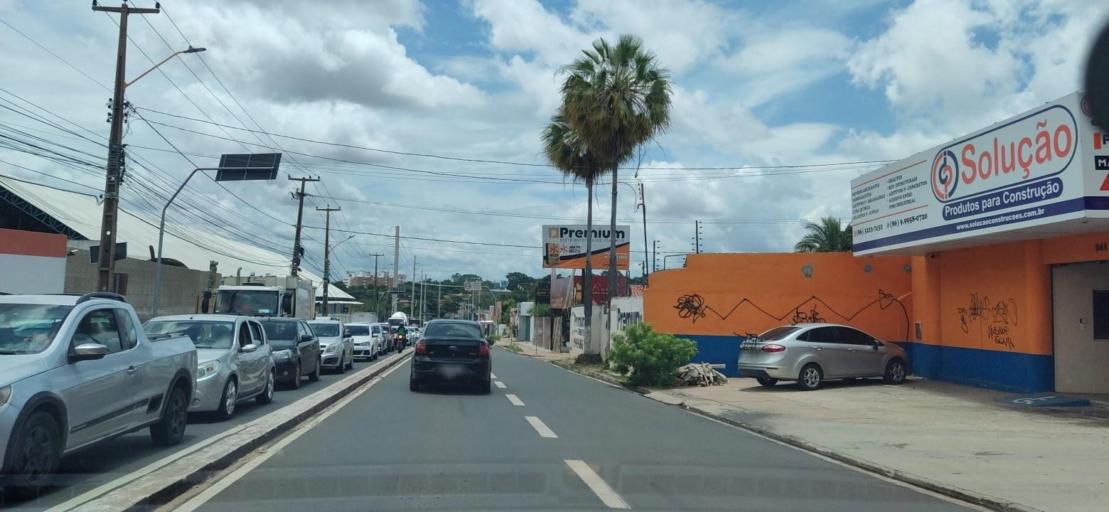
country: BR
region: Piaui
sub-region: Teresina
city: Teresina
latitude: -5.0887
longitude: -42.7626
